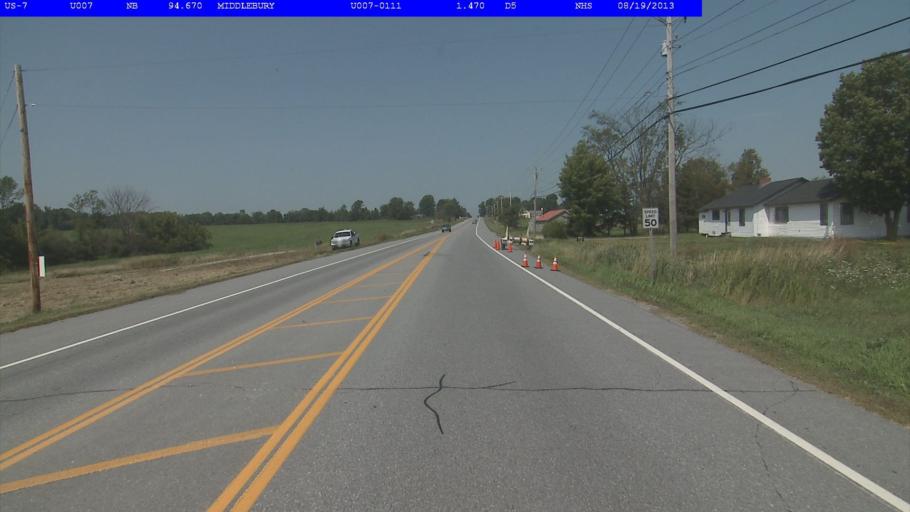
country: US
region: Vermont
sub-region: Addison County
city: Middlebury (village)
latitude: 43.9768
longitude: -73.1188
